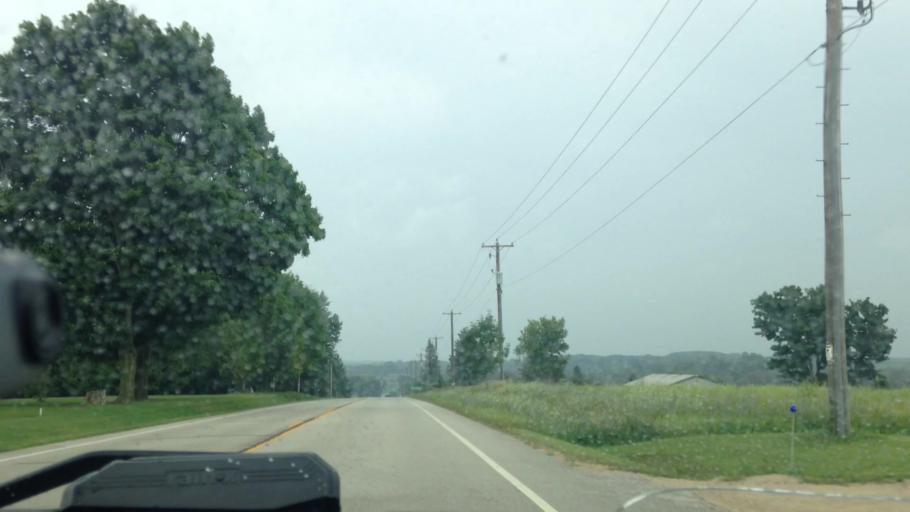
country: US
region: Wisconsin
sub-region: Washington County
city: Hartford
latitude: 43.4074
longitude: -88.3685
